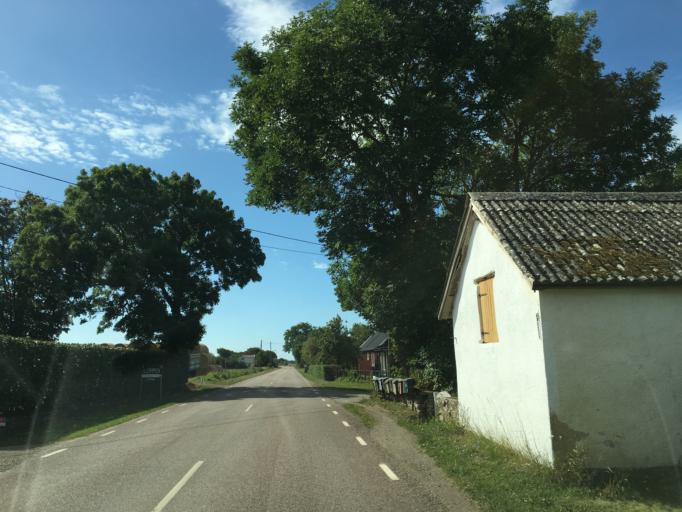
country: SE
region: Kalmar
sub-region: Morbylanga Kommun
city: Moerbylanga
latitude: 56.3897
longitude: 16.4127
